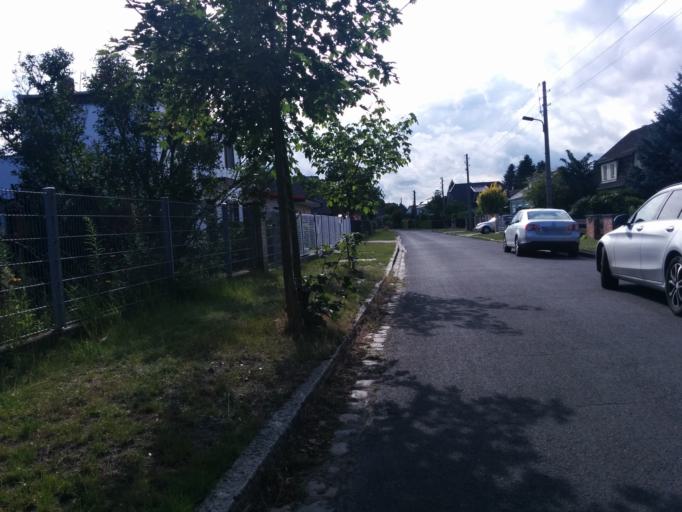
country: DE
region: Berlin
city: Biesdorf
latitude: 52.4839
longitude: 13.5720
